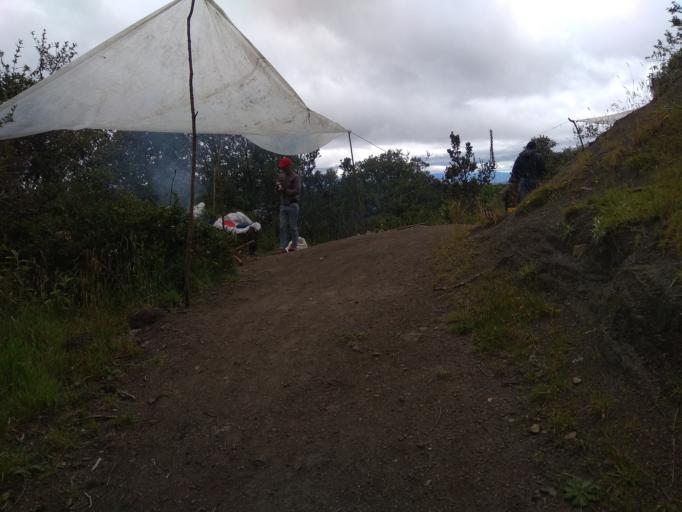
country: CO
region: Boyaca
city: Mongui
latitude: 5.7351
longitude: -72.8288
